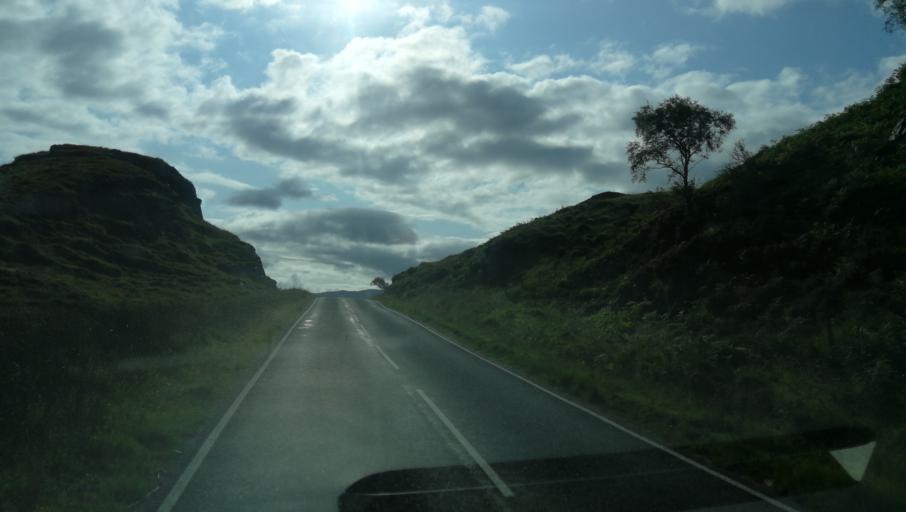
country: GB
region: Scotland
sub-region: Argyll and Bute
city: Isle Of Mull
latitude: 56.6791
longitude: -5.8488
